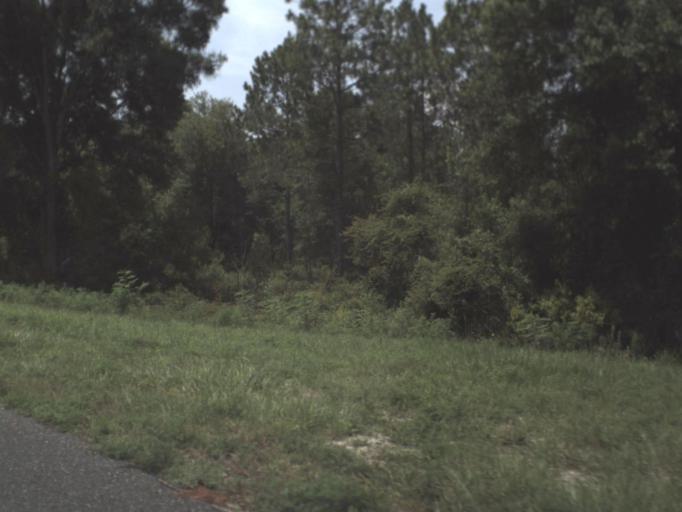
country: US
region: Florida
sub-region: Taylor County
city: Perry
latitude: 30.0434
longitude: -83.5495
